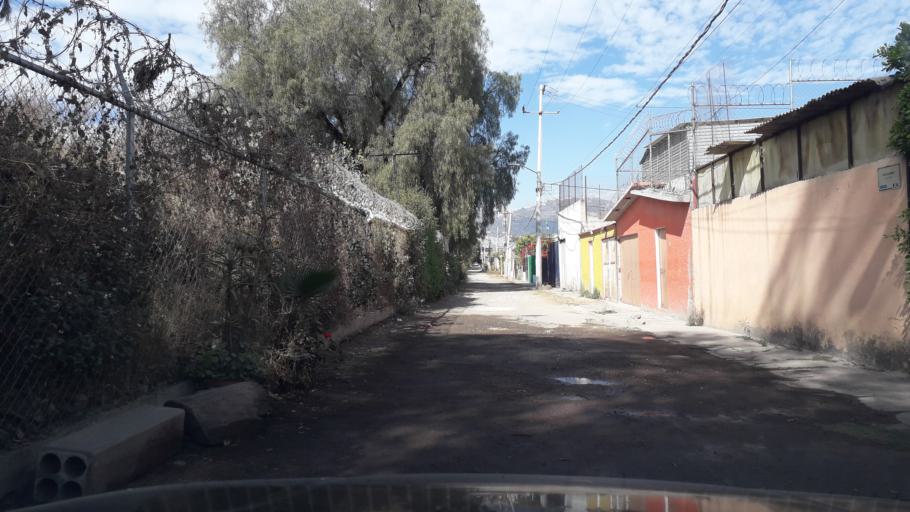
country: MX
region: Mexico City
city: Gustavo A. Madero
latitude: 19.5083
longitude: -99.0865
